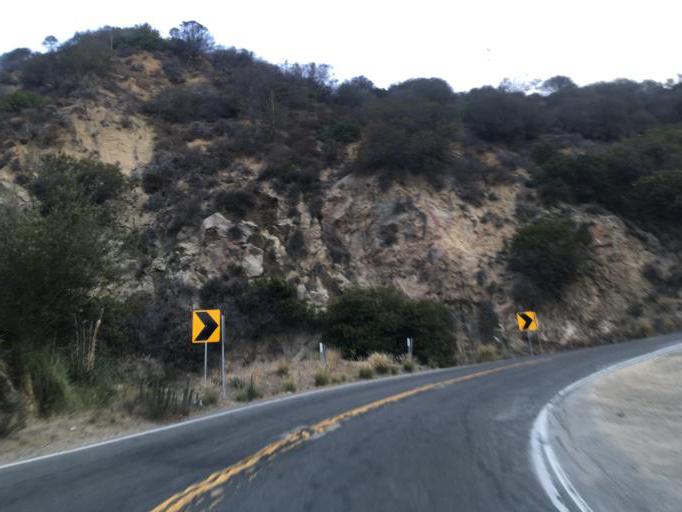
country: US
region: California
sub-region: Los Angeles County
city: Las Flores
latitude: 34.0522
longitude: -118.6394
